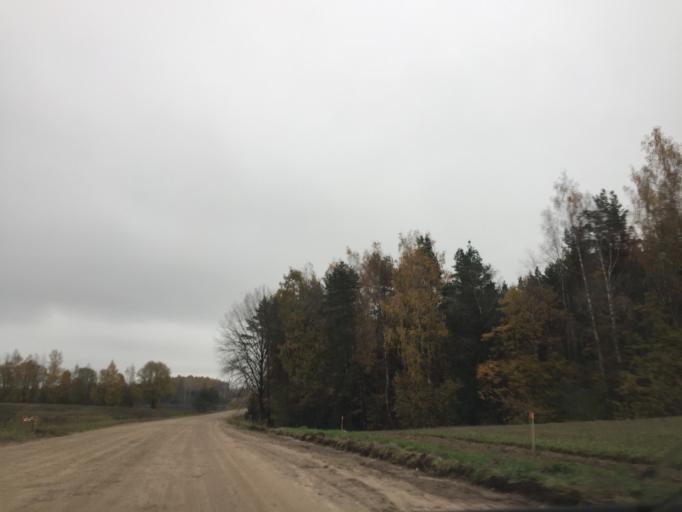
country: LV
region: Sigulda
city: Sigulda
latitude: 57.2739
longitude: 24.8434
